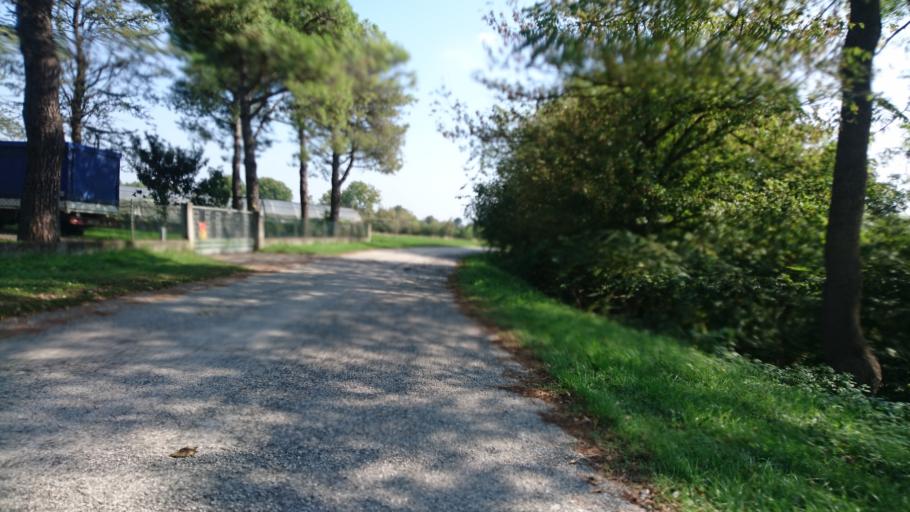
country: IT
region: Veneto
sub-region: Provincia di Padova
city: Piazzola sul Brenta
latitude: 45.5708
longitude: 11.7719
